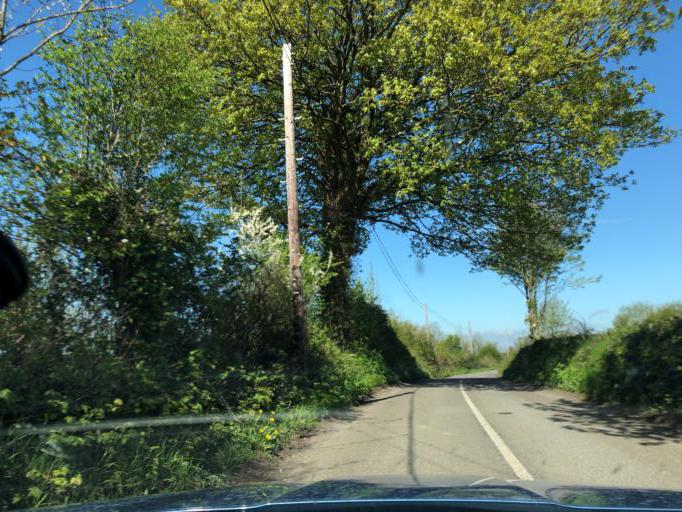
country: IE
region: Connaught
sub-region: County Galway
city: Portumna
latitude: 53.1594
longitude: -8.2565
